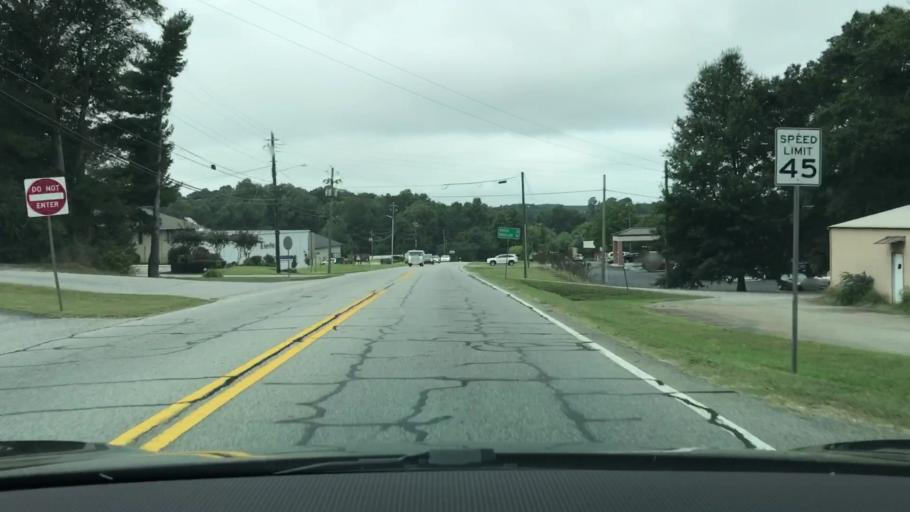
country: US
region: Georgia
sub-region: Oconee County
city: Watkinsville
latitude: 33.8657
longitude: -83.4117
